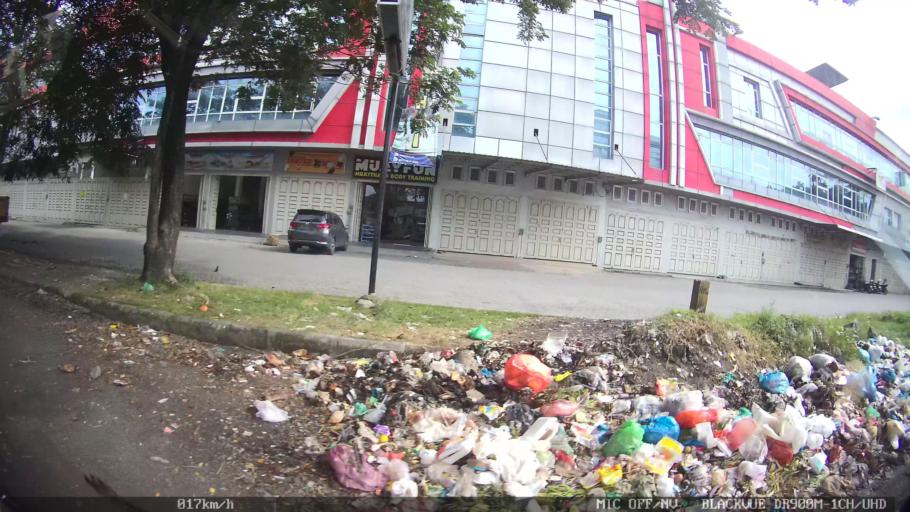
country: ID
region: North Sumatra
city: Medan
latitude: 3.6302
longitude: 98.6981
